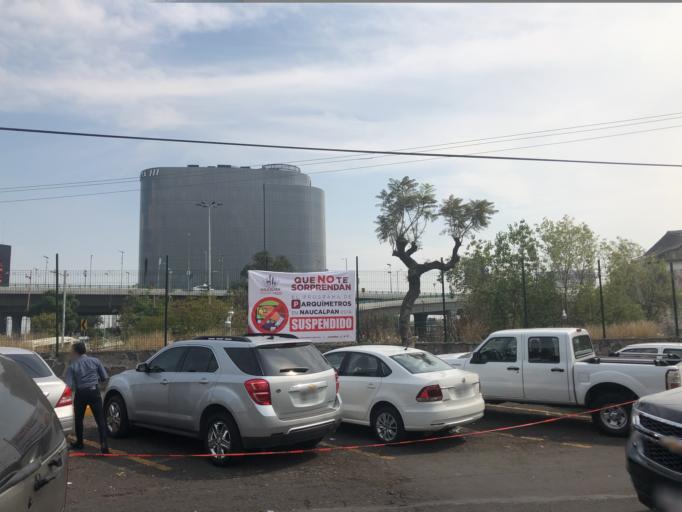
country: MX
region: Mexico
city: Naucalpan de Juarez
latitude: 19.4787
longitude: -99.2326
